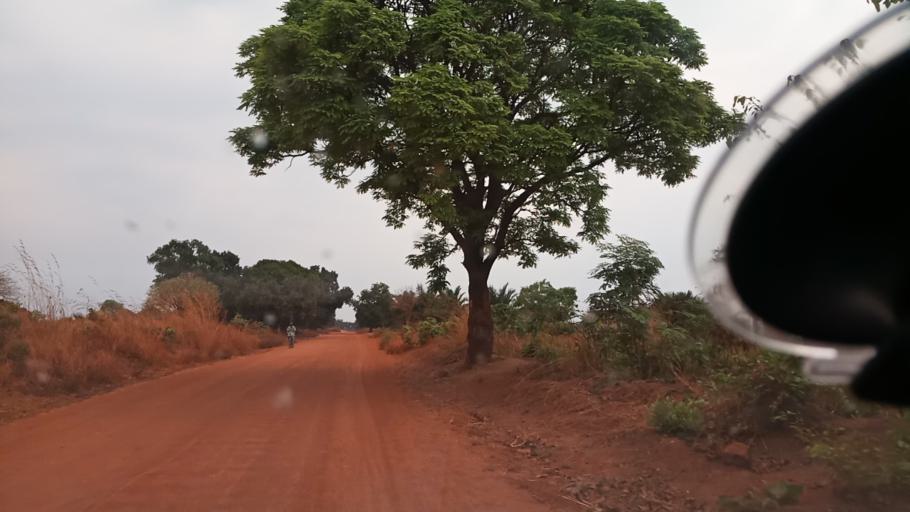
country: ZM
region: Luapula
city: Nchelenge
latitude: -9.1673
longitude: 28.2816
